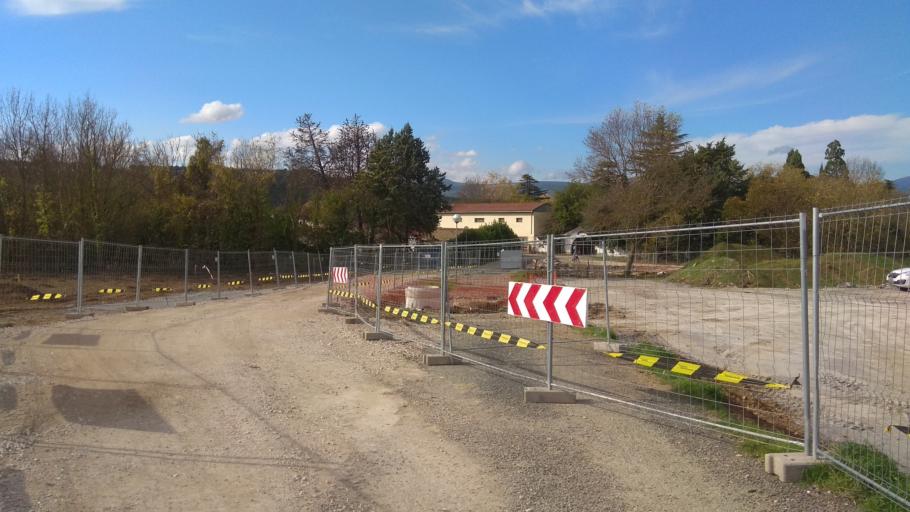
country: ES
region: Navarre
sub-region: Provincia de Navarra
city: Cizur Mayor
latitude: 42.8025
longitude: -1.6960
